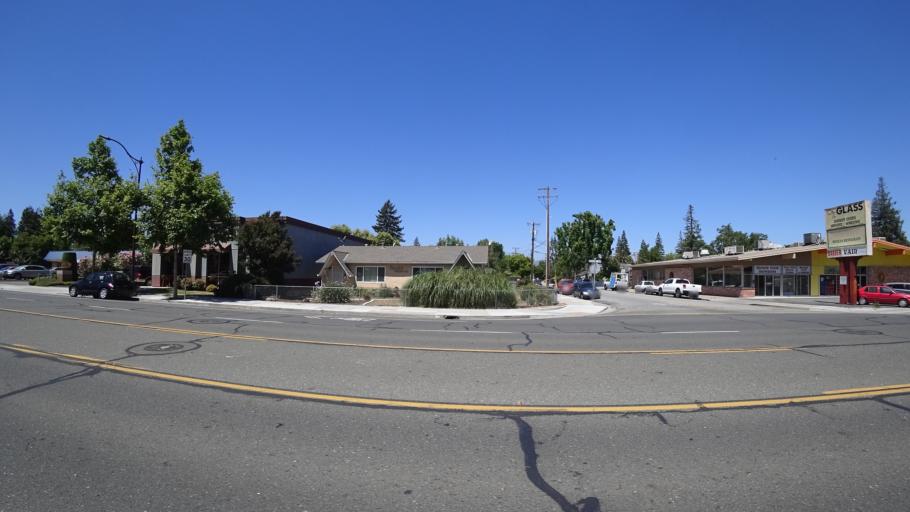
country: US
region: California
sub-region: Santa Clara County
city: Campbell
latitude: 37.2834
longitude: -121.9497
